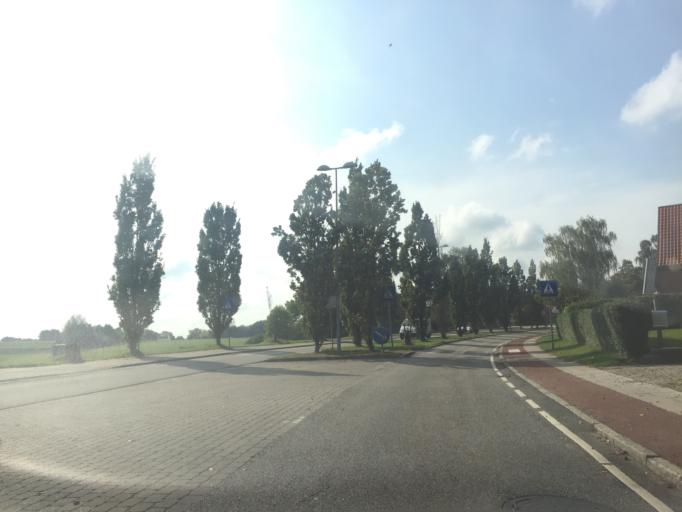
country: DK
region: Zealand
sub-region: Holbaek Kommune
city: Tollose
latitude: 55.6126
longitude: 11.7830
